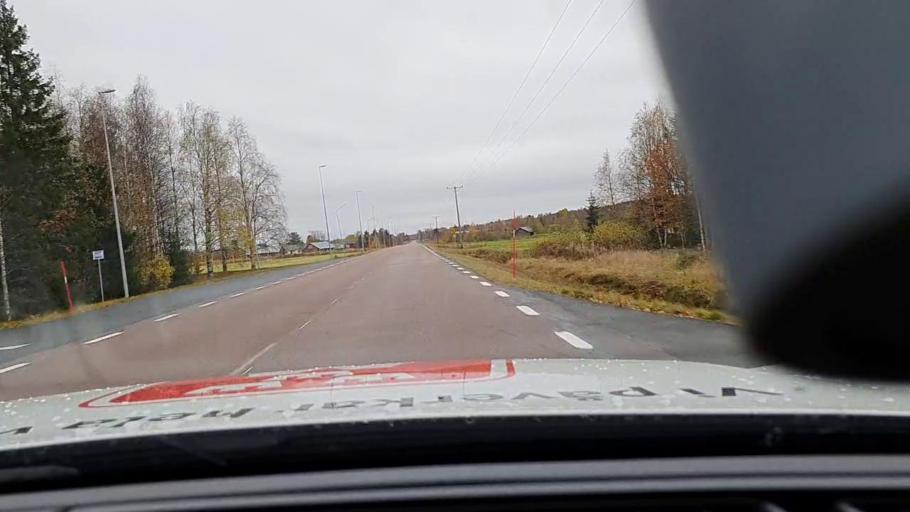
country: FI
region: Lapland
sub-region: Torniolaakso
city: Ylitornio
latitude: 66.1411
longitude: 23.8993
